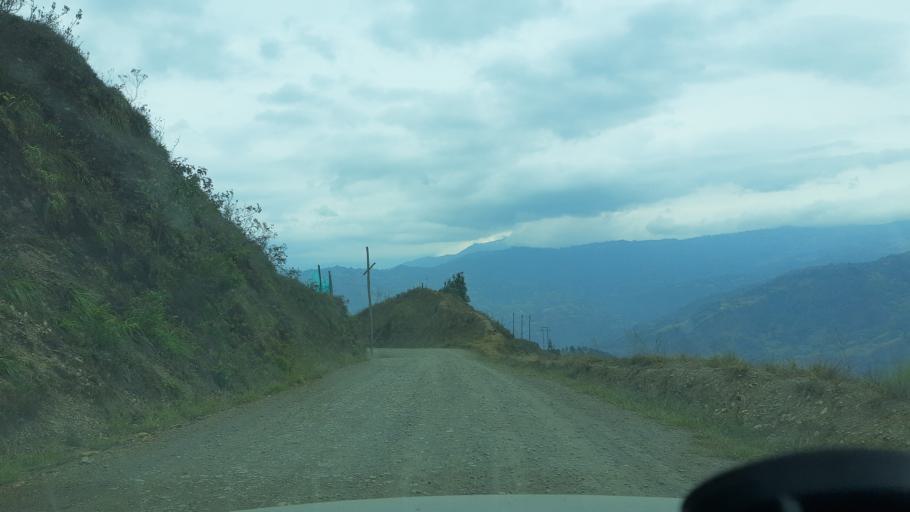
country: CO
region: Boyaca
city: Somondoco
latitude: 4.9813
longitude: -73.3755
